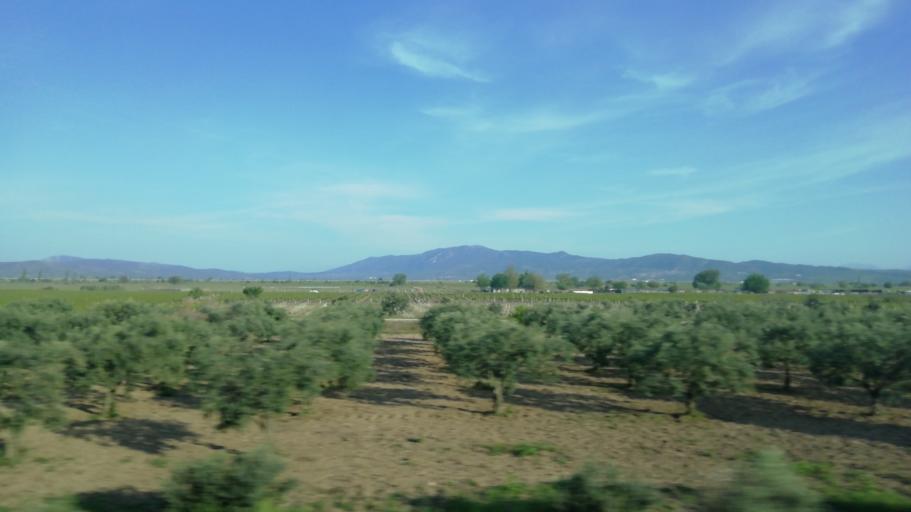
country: TR
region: Manisa
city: Saruhanli
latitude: 38.7616
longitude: 27.6439
